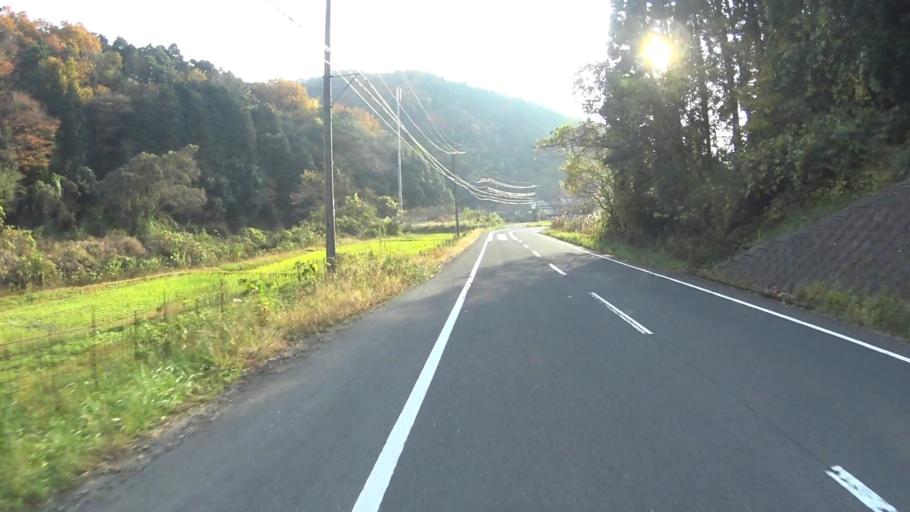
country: JP
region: Kyoto
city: Maizuru
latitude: 35.5093
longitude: 135.4527
